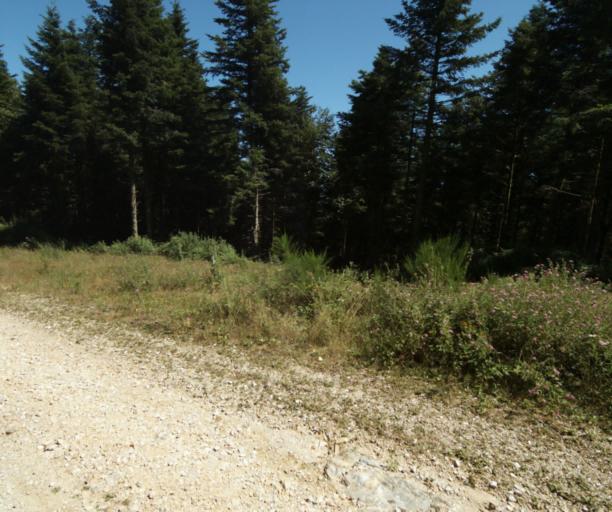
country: FR
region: Midi-Pyrenees
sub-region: Departement du Tarn
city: Dourgne
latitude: 43.4524
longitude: 2.1595
